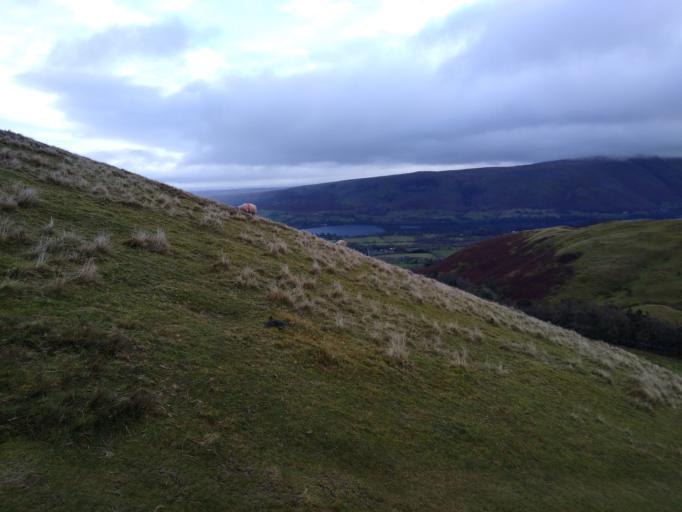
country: GB
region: England
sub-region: Cumbria
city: Penrith
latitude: 54.6061
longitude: -2.8954
